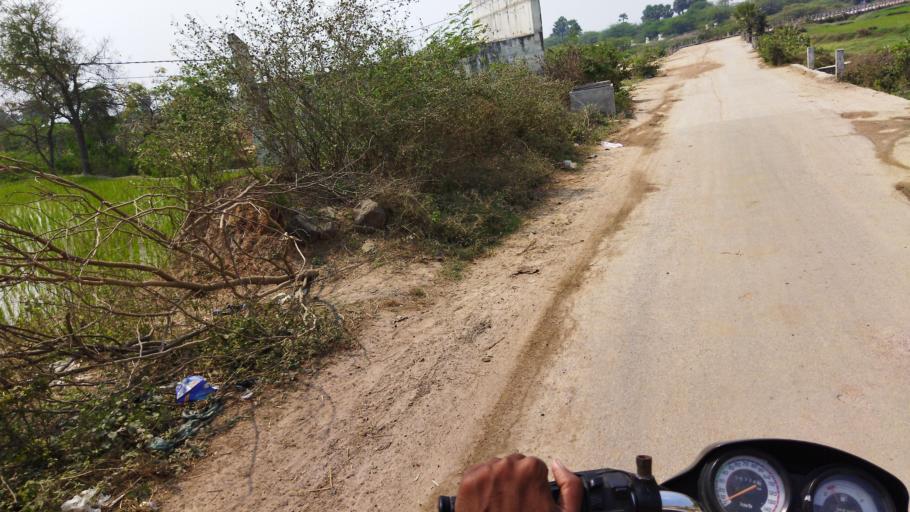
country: IN
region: Telangana
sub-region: Nalgonda
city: Nalgonda
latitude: 17.1405
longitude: 79.3888
